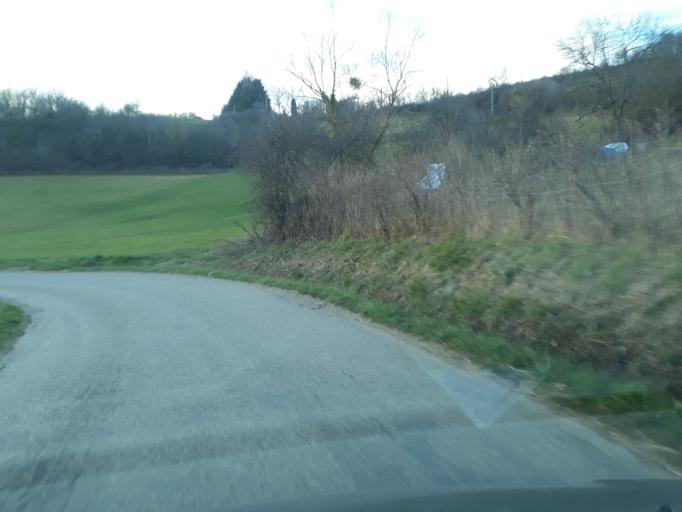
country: FR
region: Midi-Pyrenees
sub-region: Departement de la Haute-Garonne
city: Montesquieu-Volvestre
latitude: 43.1698
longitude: 1.3175
